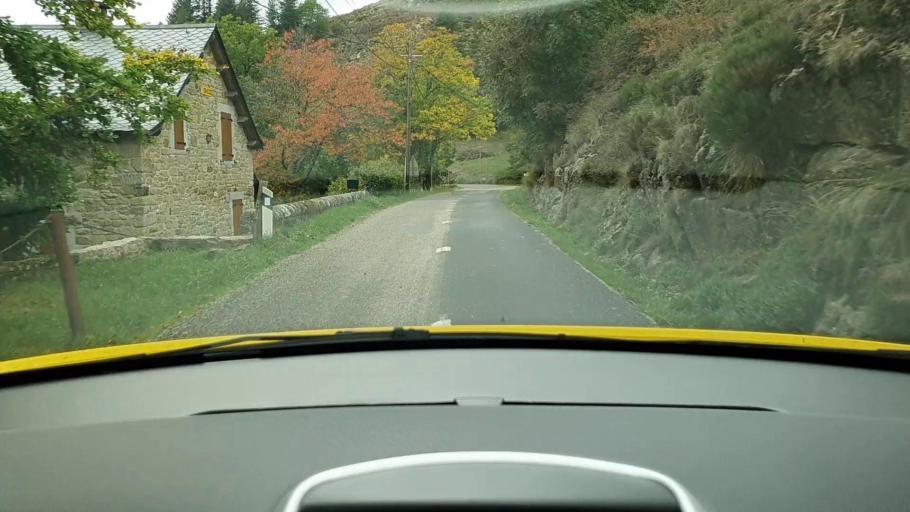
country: FR
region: Languedoc-Roussillon
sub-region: Departement de la Lozere
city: Meyrueis
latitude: 44.0765
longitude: 3.4861
